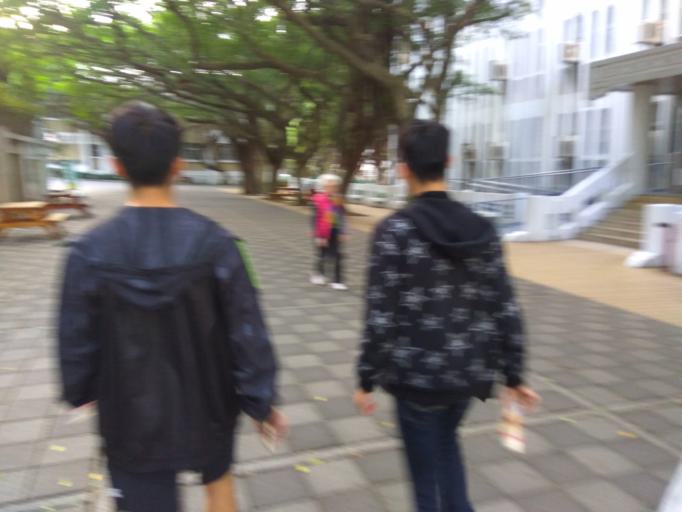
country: TW
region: Taipei
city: Taipei
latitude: 25.1760
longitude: 121.4497
